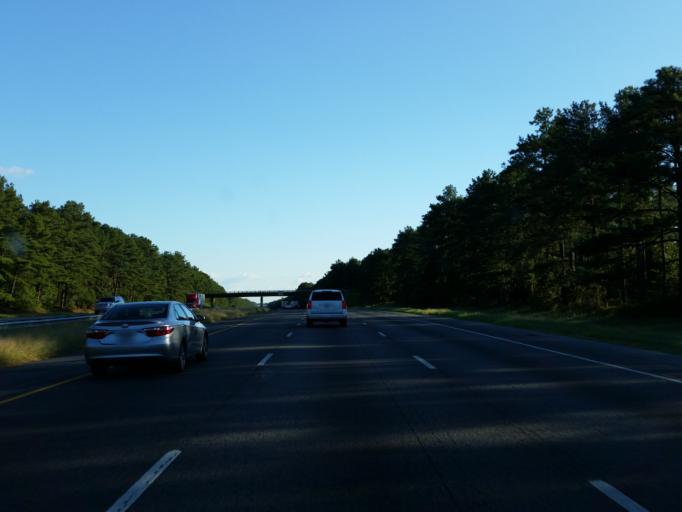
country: US
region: Georgia
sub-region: Houston County
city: Perry
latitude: 32.3850
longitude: -83.7681
